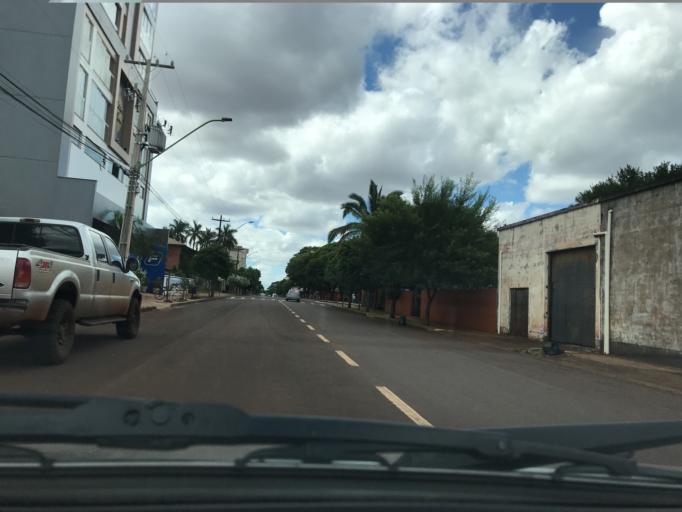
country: BR
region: Parana
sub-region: Palotina
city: Palotina
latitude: -24.2868
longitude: -53.8376
